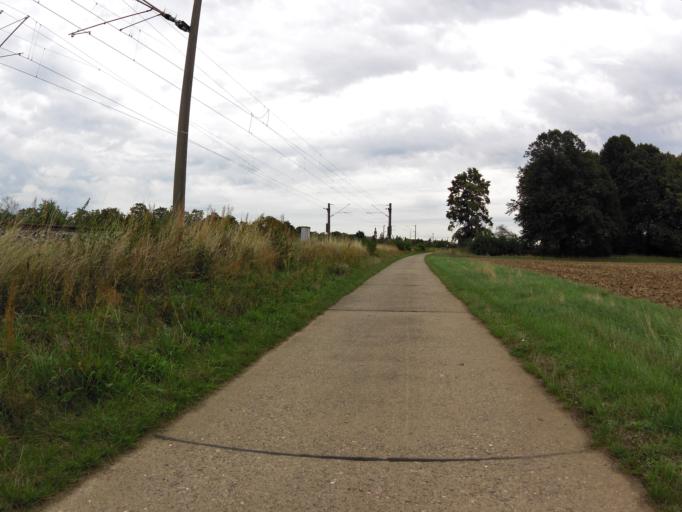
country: DE
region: Bavaria
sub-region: Regierungsbezirk Unterfranken
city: Donnersdorf
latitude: 50.0167
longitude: 10.4058
